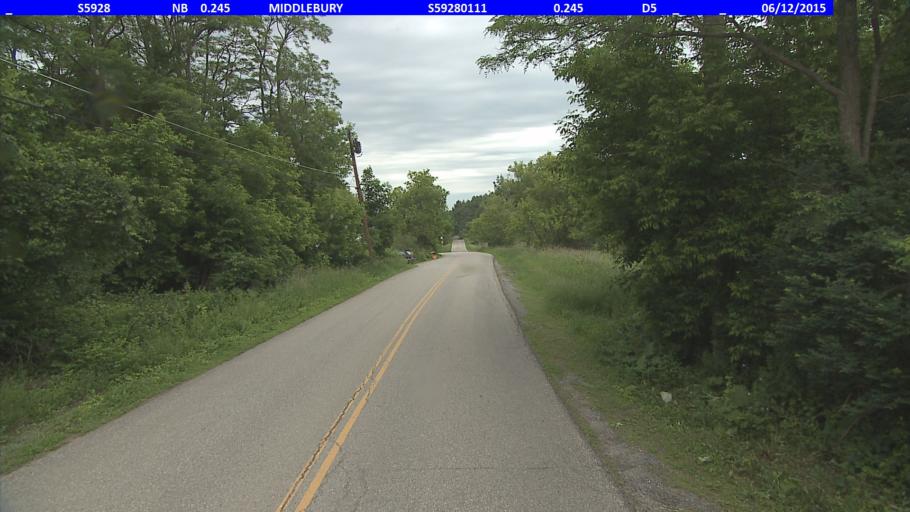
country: US
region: Vermont
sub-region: Addison County
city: Middlebury (village)
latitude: 44.0279
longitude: -73.1770
